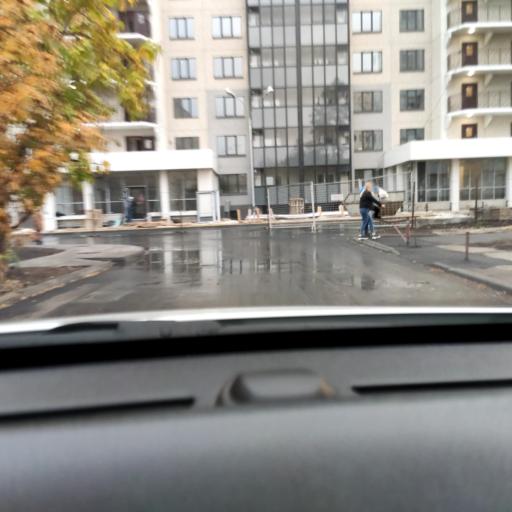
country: RU
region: Voronezj
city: Somovo
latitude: 51.6884
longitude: 39.2858
